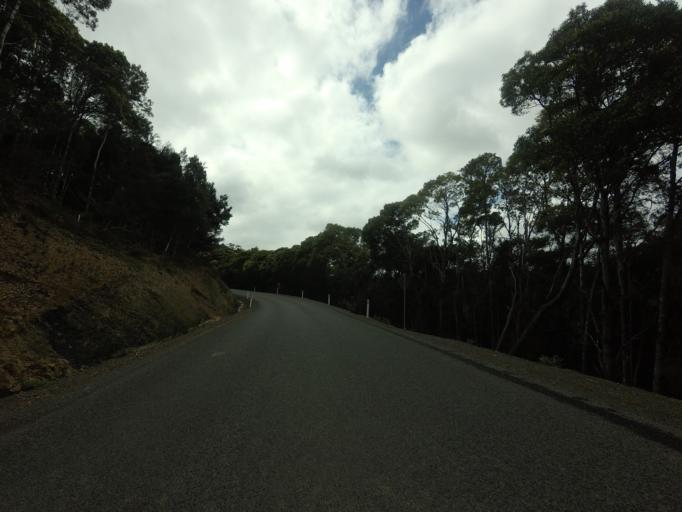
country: AU
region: Tasmania
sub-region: Huon Valley
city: Geeveston
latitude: -43.4295
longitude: 146.9048
